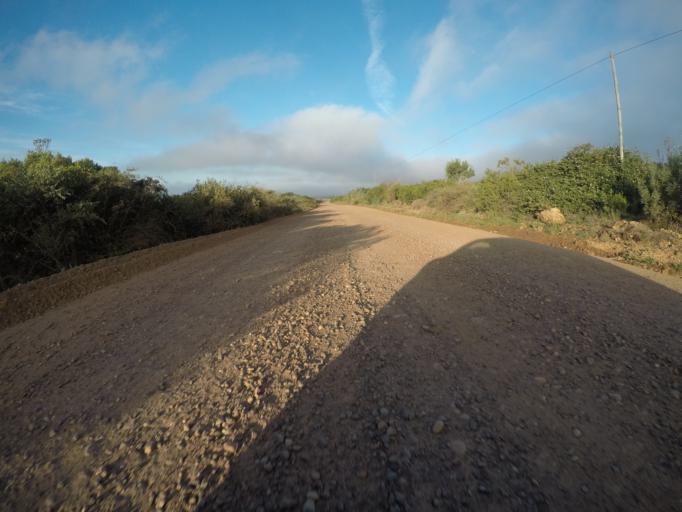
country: ZA
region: Western Cape
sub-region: Eden District Municipality
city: Mossel Bay
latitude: -34.1444
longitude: 22.0204
